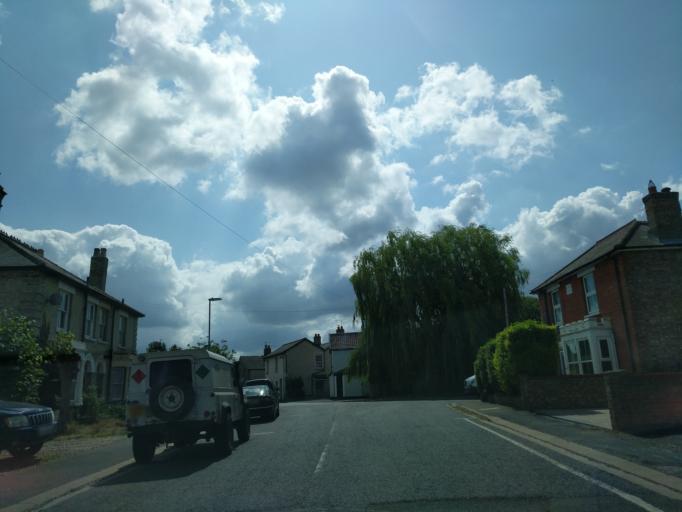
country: GB
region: England
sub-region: Cambridgeshire
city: Isleham
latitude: 52.3121
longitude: 0.3847
